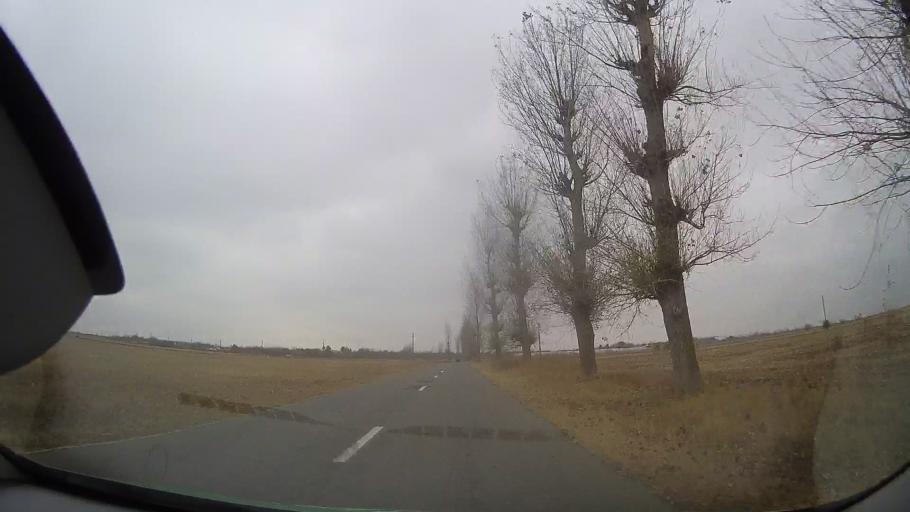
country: RO
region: Ialomita
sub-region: Comuna Valea Macrisului
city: Valea Macrisului
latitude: 44.7373
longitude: 26.8467
